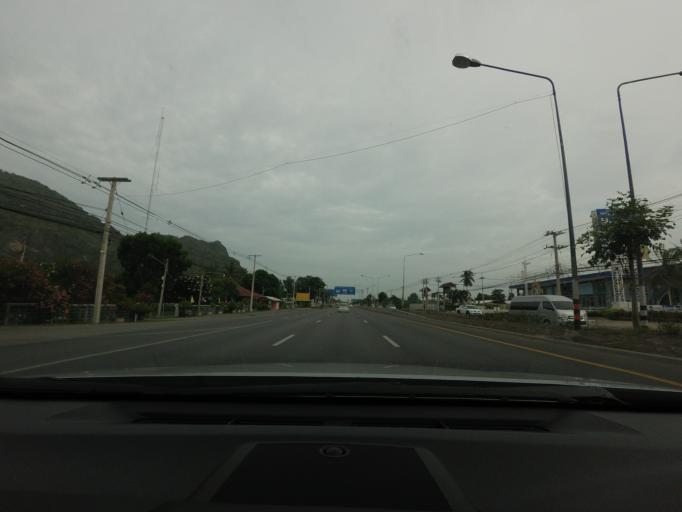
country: TH
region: Phetchaburi
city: Cha-am
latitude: 12.8287
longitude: 99.9357
